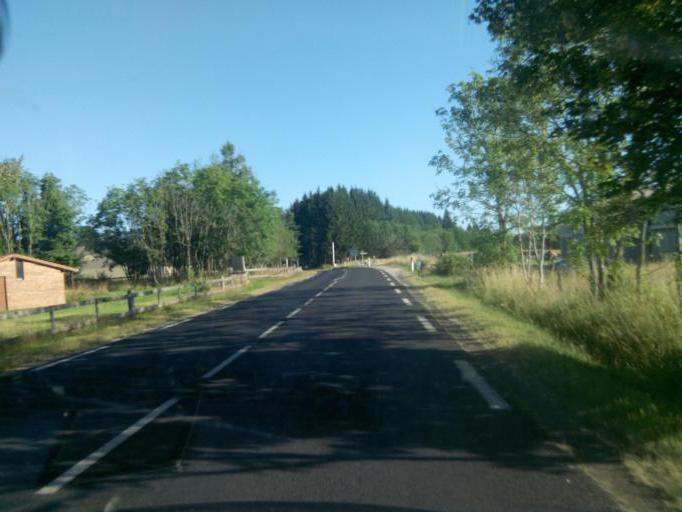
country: FR
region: Auvergne
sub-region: Departement de la Haute-Loire
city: Fontannes
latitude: 45.3106
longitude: 3.6985
